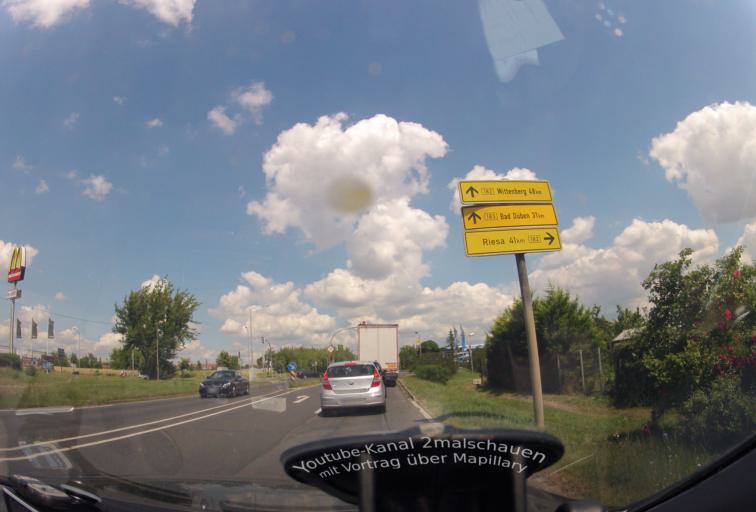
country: DE
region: Saxony
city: Zinna
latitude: 51.5611
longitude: 12.9719
